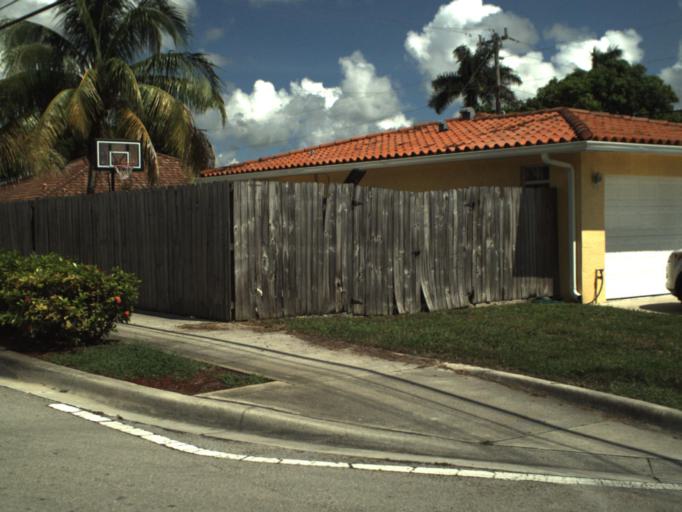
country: US
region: Florida
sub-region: Broward County
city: Miramar
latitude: 25.9938
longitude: -80.2743
